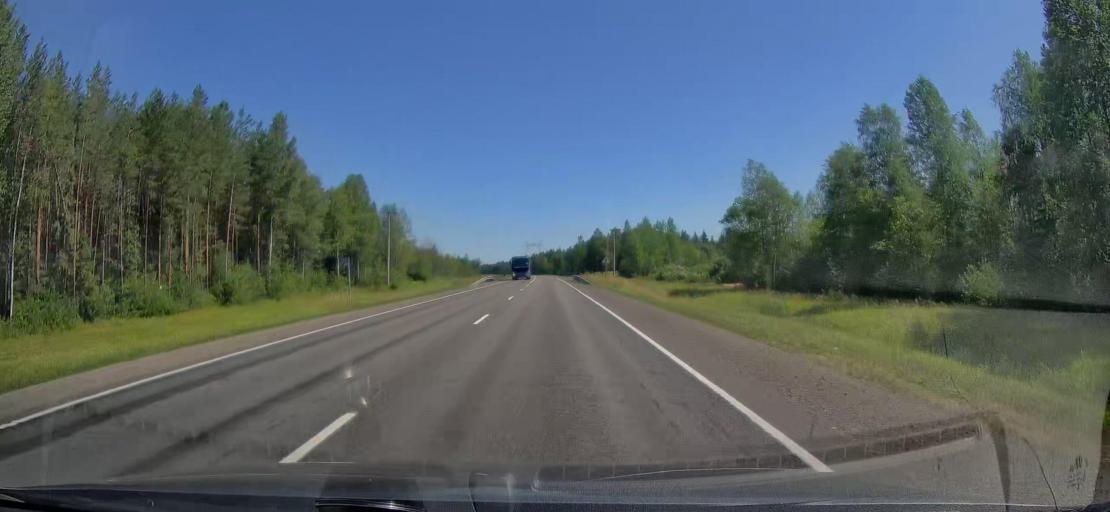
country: RU
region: Tverskaya
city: Ves'yegonsk
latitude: 58.9217
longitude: 37.2156
